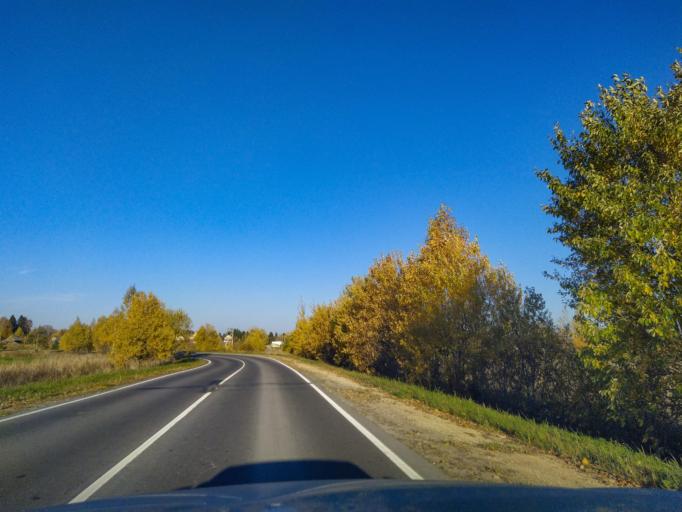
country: RU
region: Leningrad
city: Siverskiy
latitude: 59.3192
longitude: 30.0388
